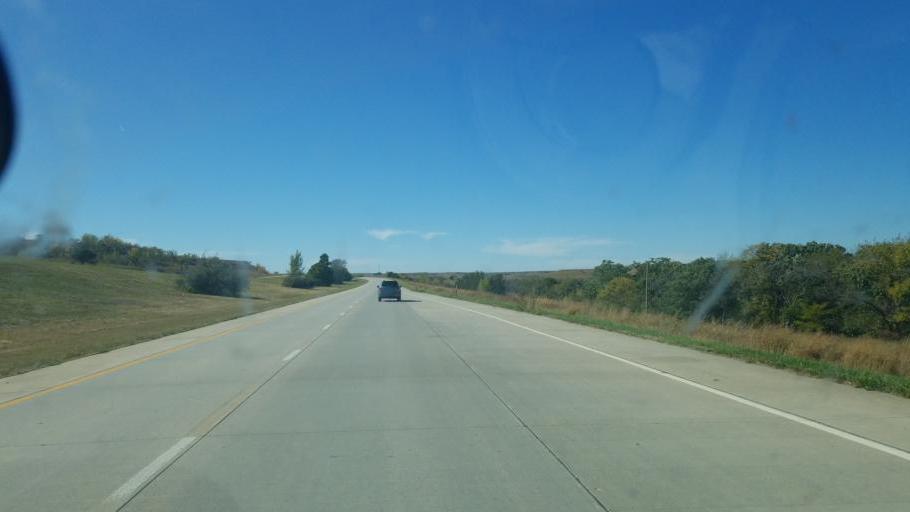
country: US
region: Kansas
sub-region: Riley County
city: Ogden
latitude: 39.0670
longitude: -96.6268
